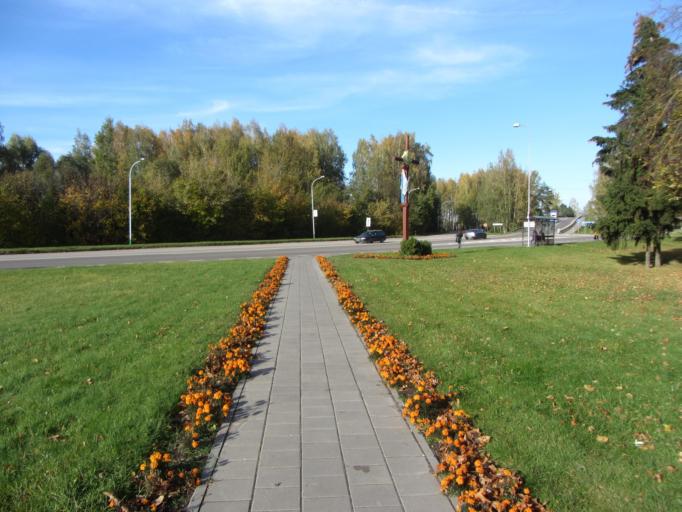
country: LT
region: Vilnius County
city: Elektrenai
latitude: 54.7881
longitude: 24.6587
